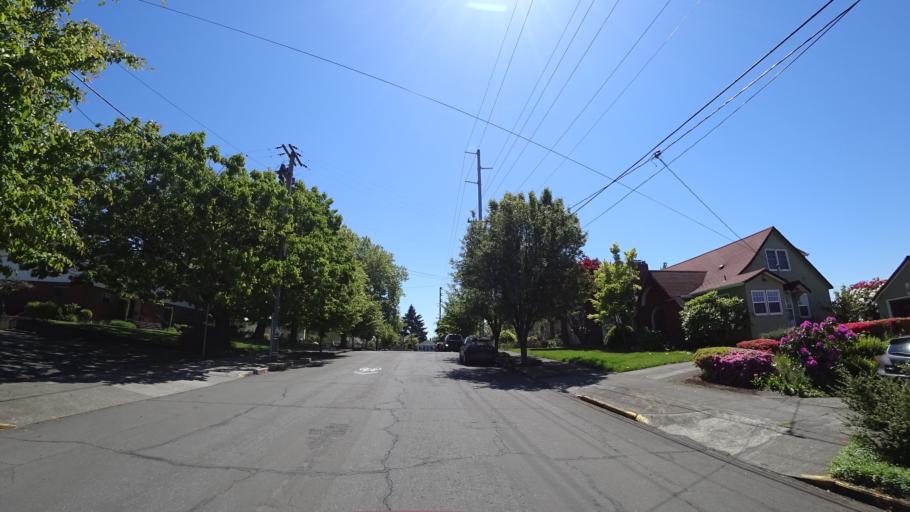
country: US
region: Oregon
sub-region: Multnomah County
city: Lents
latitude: 45.4986
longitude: -122.6186
